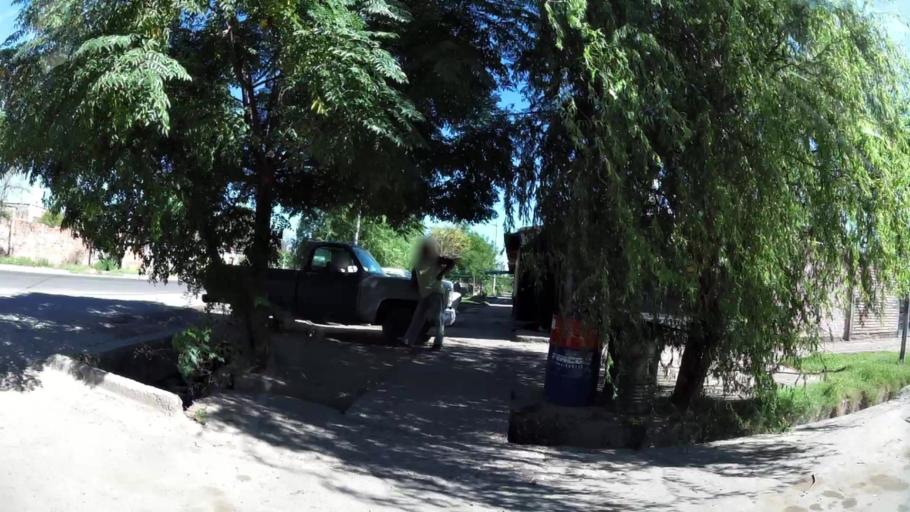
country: AR
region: Mendoza
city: Las Heras
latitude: -32.8389
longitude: -68.8109
